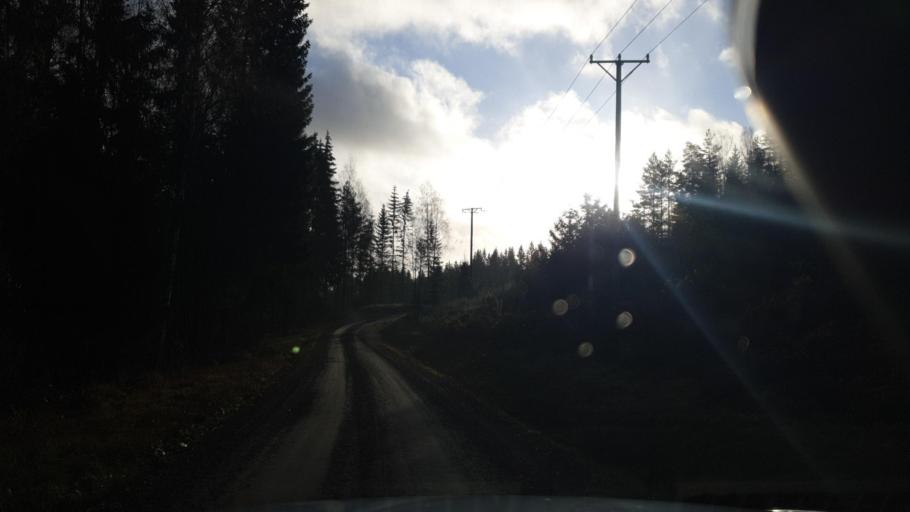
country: SE
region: Vaermland
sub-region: Grums Kommun
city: Grums
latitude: 59.4977
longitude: 12.9245
